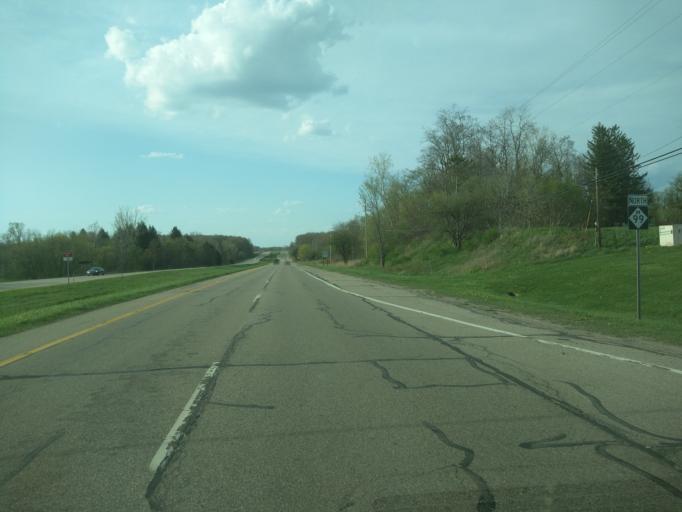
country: US
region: Michigan
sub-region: Eaton County
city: Dimondale
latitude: 42.6261
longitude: -84.6226
